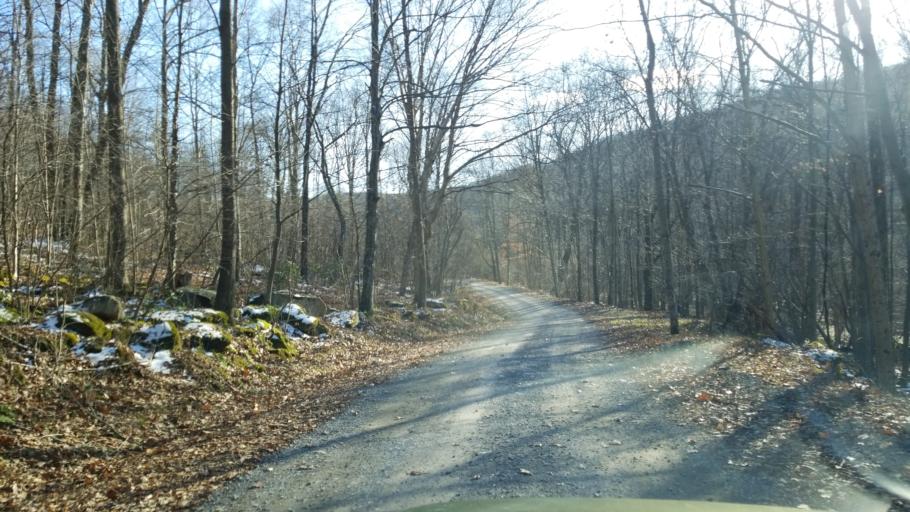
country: US
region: Pennsylvania
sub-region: Jefferson County
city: Brockway
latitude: 41.2831
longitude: -78.8264
